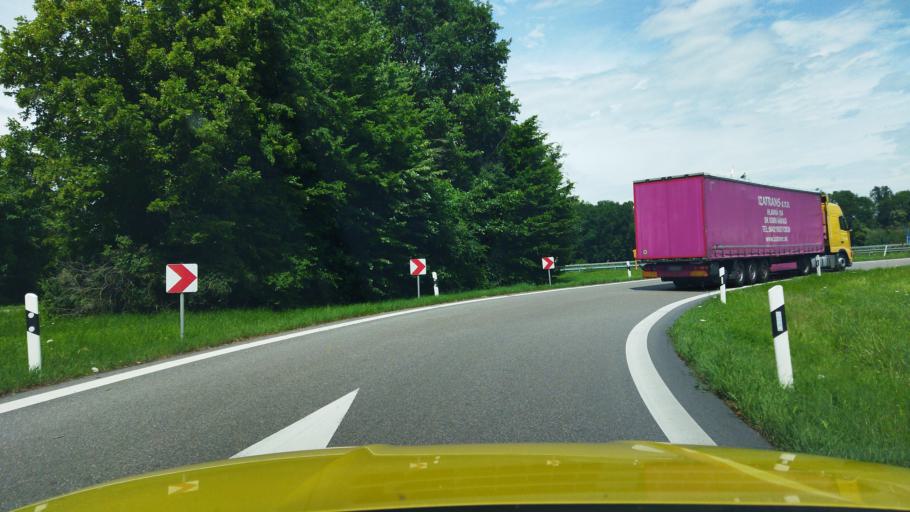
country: DE
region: Baden-Wuerttemberg
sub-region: Regierungsbezirk Stuttgart
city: Kirchberg an der Jagst
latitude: 49.1768
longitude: 9.9588
